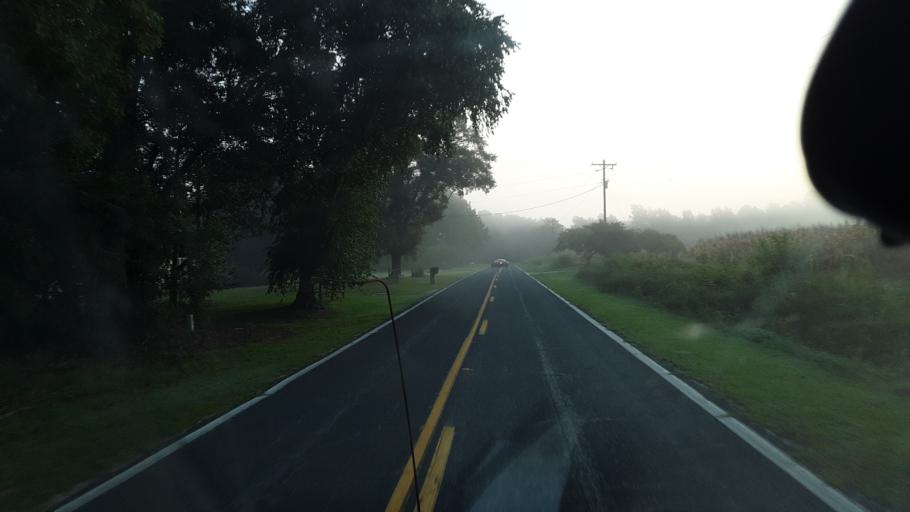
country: US
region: South Carolina
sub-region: Clarendon County
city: Manning
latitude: 33.7180
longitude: -80.1334
